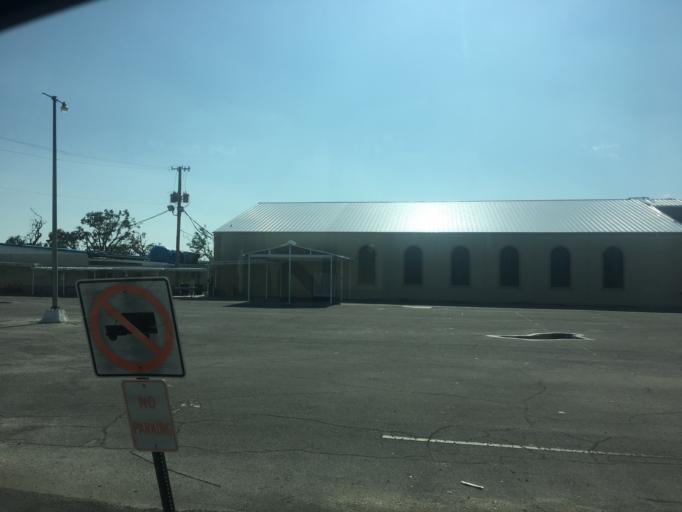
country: US
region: Florida
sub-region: Bay County
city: Springfield
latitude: 30.1602
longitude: -85.6079
